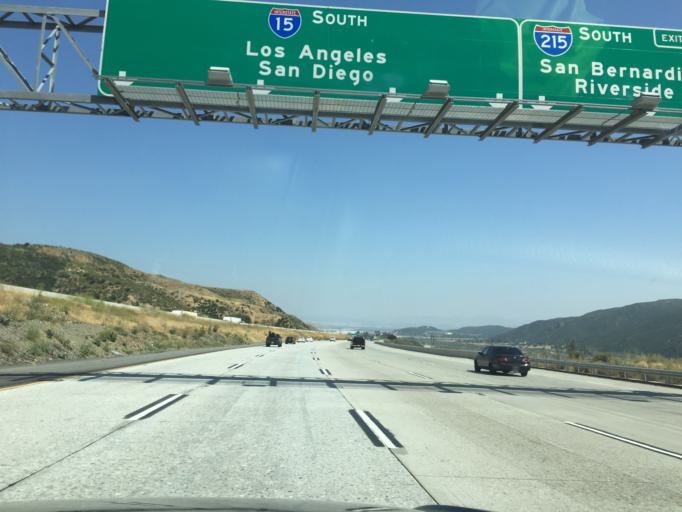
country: US
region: California
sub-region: San Bernardino County
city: Muscoy
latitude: 34.2470
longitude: -117.4380
